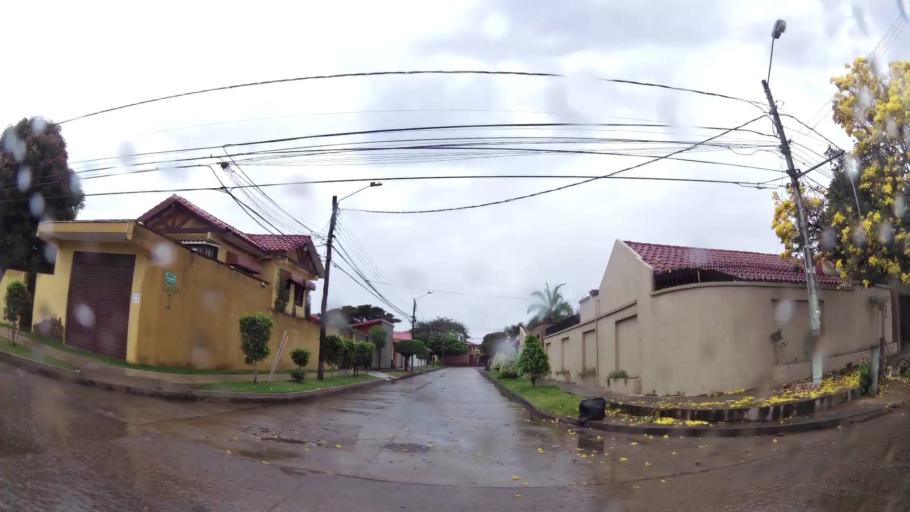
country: BO
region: Santa Cruz
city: Santa Cruz de la Sierra
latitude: -17.8053
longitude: -63.1549
